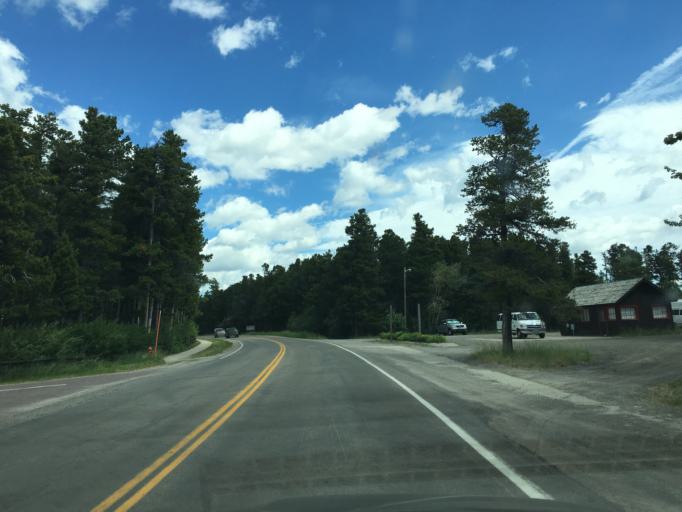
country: US
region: Montana
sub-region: Glacier County
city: South Browning
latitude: 48.4430
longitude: -113.2205
